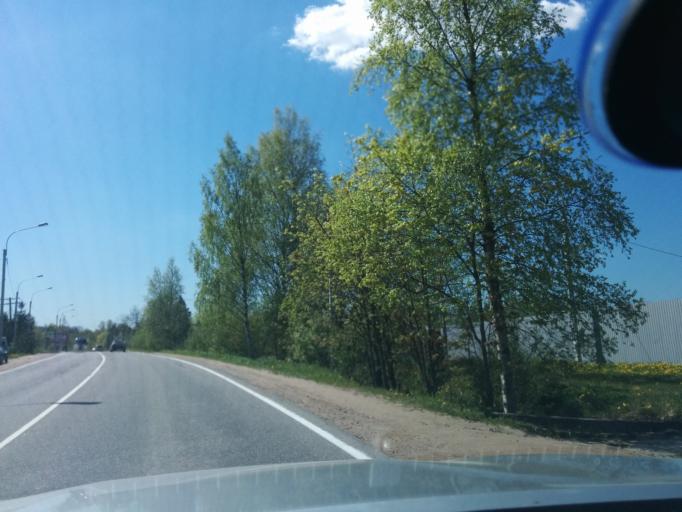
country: RU
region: Leningrad
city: Verkhniye Osel'ki
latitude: 60.2500
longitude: 30.4472
